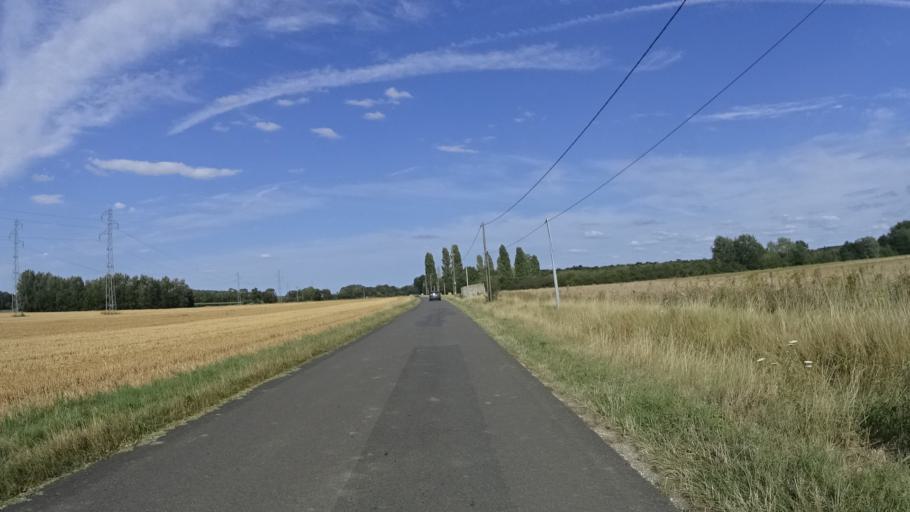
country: FR
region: Centre
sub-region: Departement du Loir-et-Cher
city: Onzain
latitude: 47.4859
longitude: 1.1501
